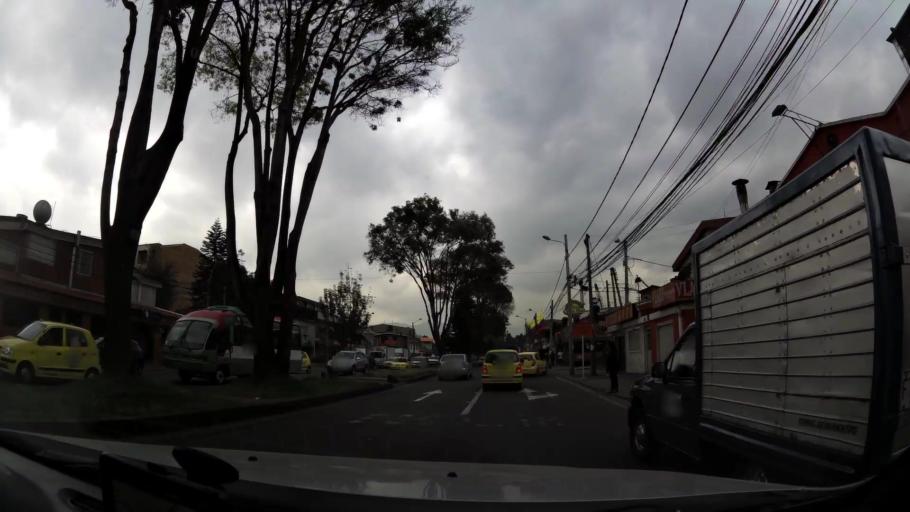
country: CO
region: Bogota D.C.
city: Bogota
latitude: 4.6706
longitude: -74.1062
